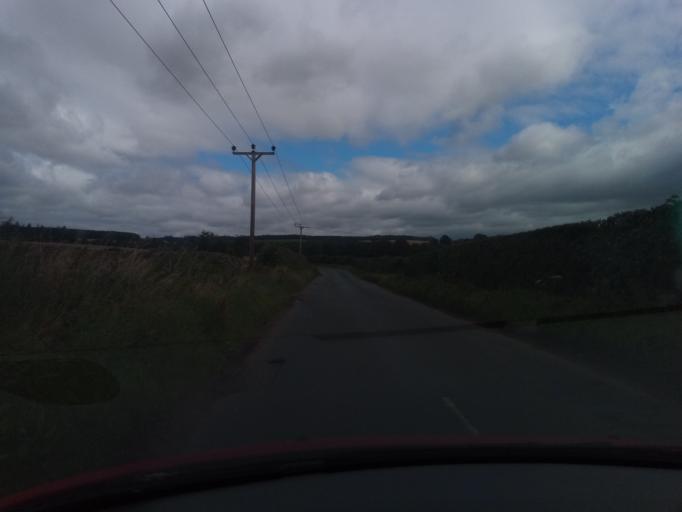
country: GB
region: Scotland
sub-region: The Scottish Borders
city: Kelso
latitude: 55.5327
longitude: -2.4554
